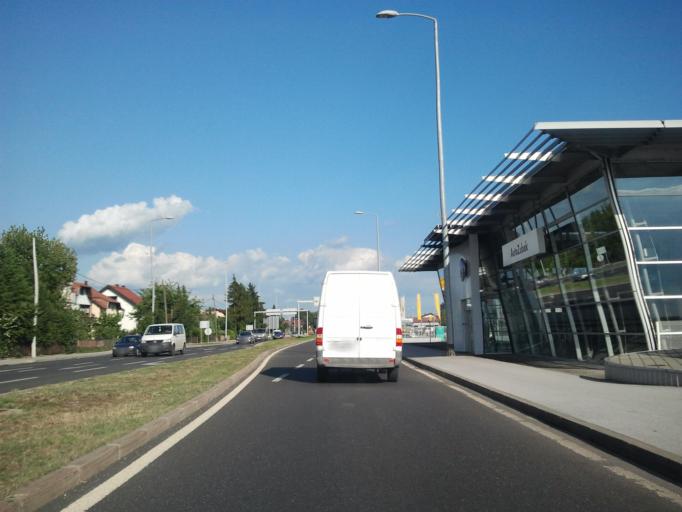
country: HR
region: Zagrebacka
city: Gradici
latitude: 45.7218
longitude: 16.0514
